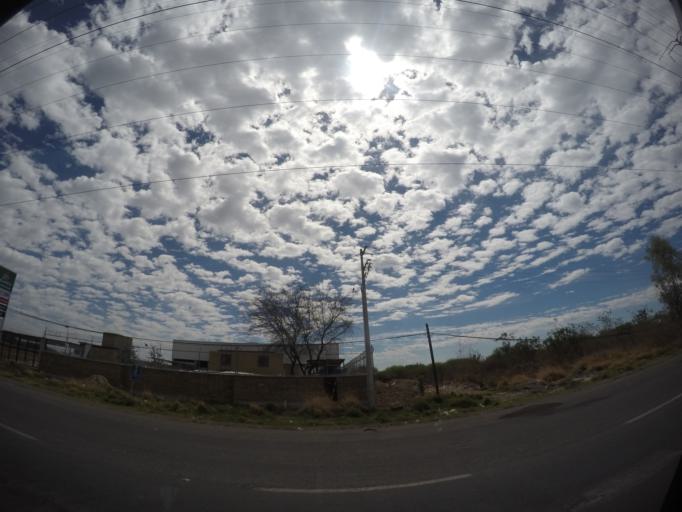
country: MX
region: Guanajuato
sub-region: Leon
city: El CERESO
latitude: 21.0239
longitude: -101.6916
